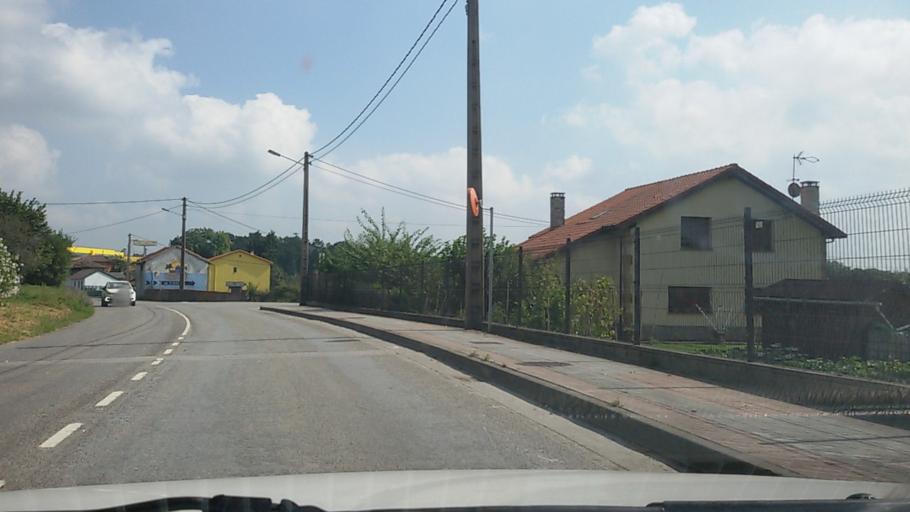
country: ES
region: Asturias
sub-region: Province of Asturias
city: Lugones
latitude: 43.4402
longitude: -5.8077
